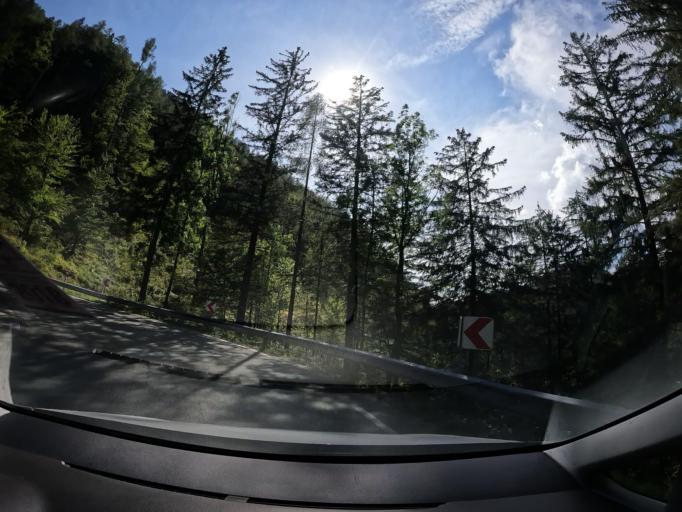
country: AT
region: Carinthia
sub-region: Politischer Bezirk Villach Land
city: Sankt Jakob
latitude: 46.5264
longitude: 14.0937
